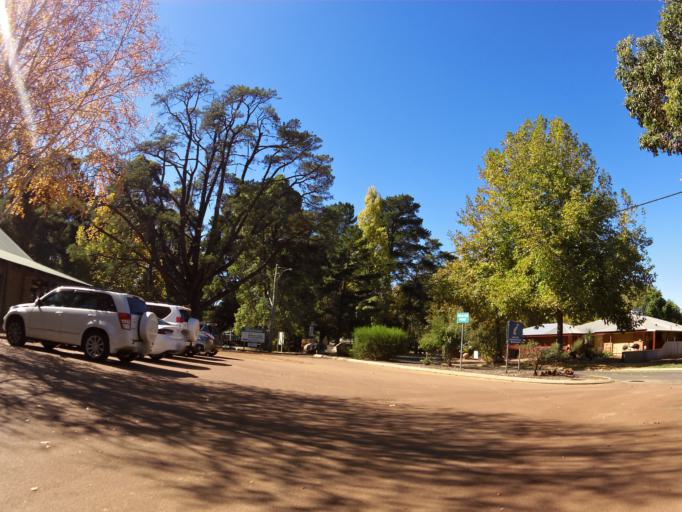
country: AU
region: Western Australia
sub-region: Waroona
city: Waroona
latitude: -32.7126
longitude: 116.0623
